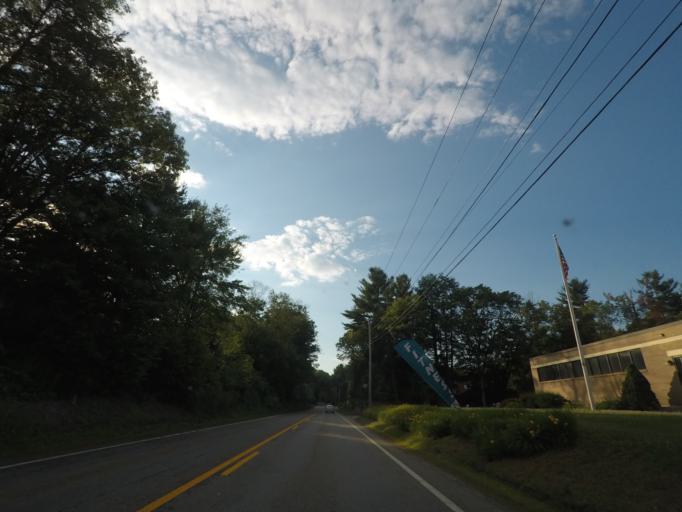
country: US
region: Connecticut
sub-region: Windham County
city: Quinebaug
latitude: 42.0317
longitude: -71.9649
